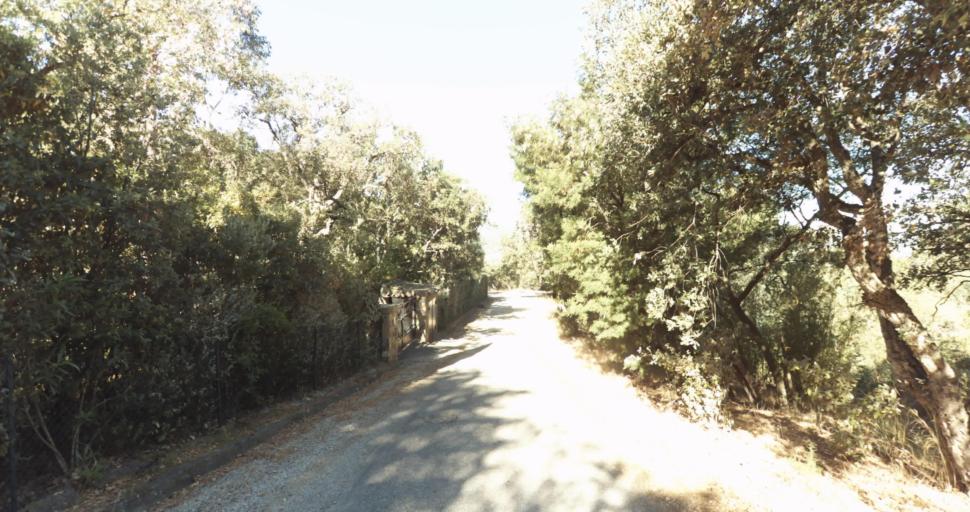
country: FR
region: Provence-Alpes-Cote d'Azur
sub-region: Departement du Var
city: Gassin
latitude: 43.2191
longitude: 6.5930
